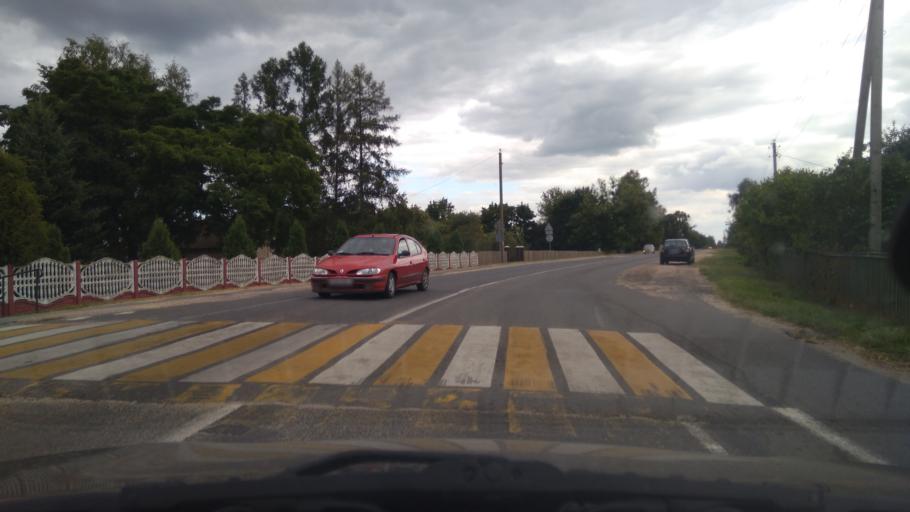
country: BY
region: Brest
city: Byelaazyorsk
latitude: 52.4998
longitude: 25.1900
